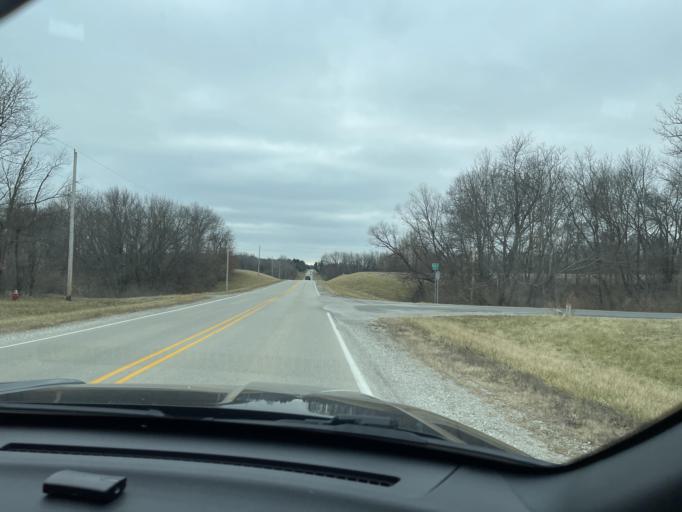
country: US
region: Illinois
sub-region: Sangamon County
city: Leland Grove
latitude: 39.8149
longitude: -89.7396
